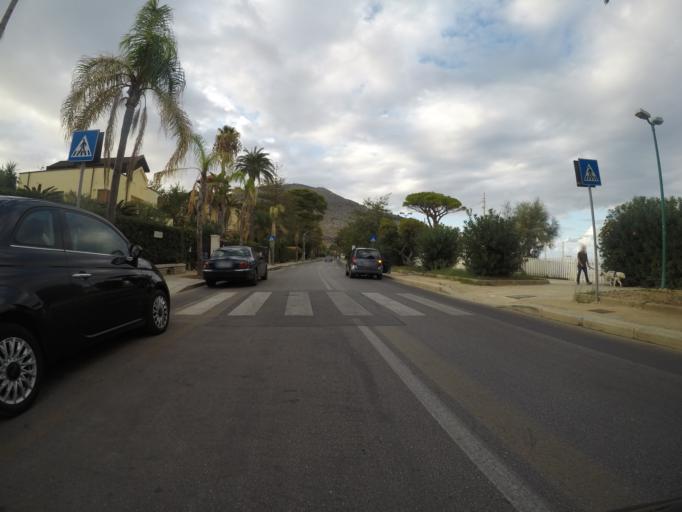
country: IT
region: Sicily
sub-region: Palermo
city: Palermo
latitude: 38.2005
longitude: 13.3275
